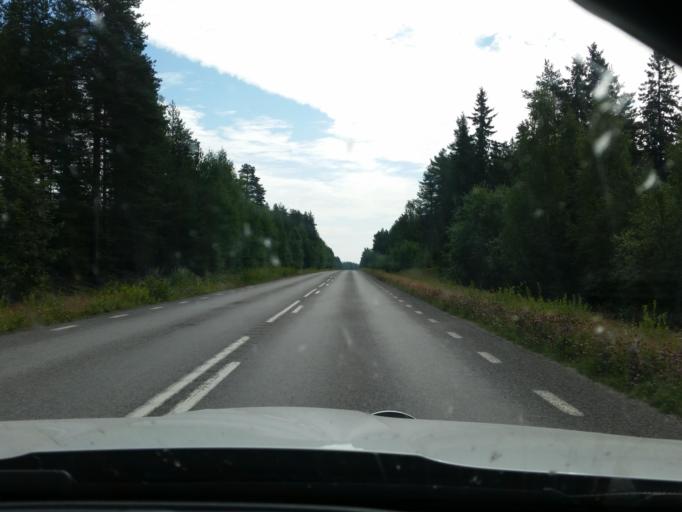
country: SE
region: Norrbotten
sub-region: Alvsbyns Kommun
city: AElvsbyn
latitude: 65.6814
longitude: 20.7993
